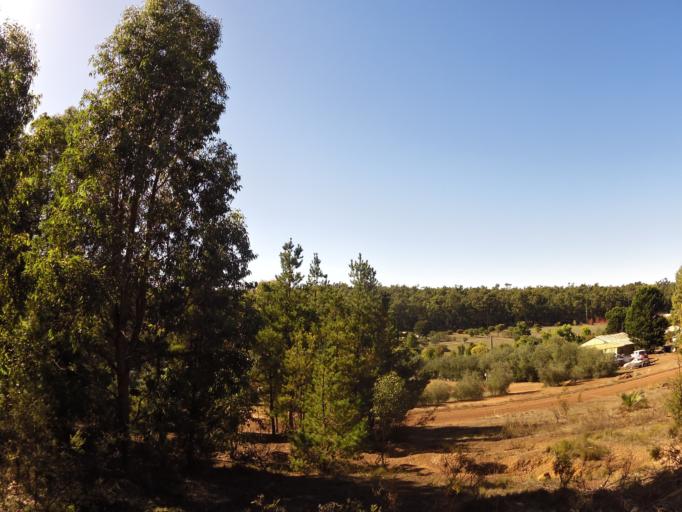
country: AU
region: Western Australia
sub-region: Waroona
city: Waroona
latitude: -32.7101
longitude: 116.0713
